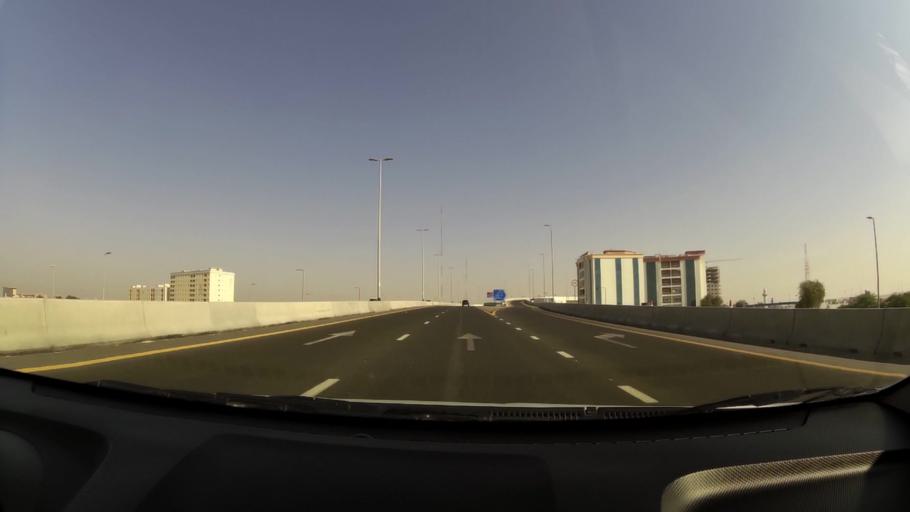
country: AE
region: Umm al Qaywayn
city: Umm al Qaywayn
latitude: 25.4963
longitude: 55.5522
